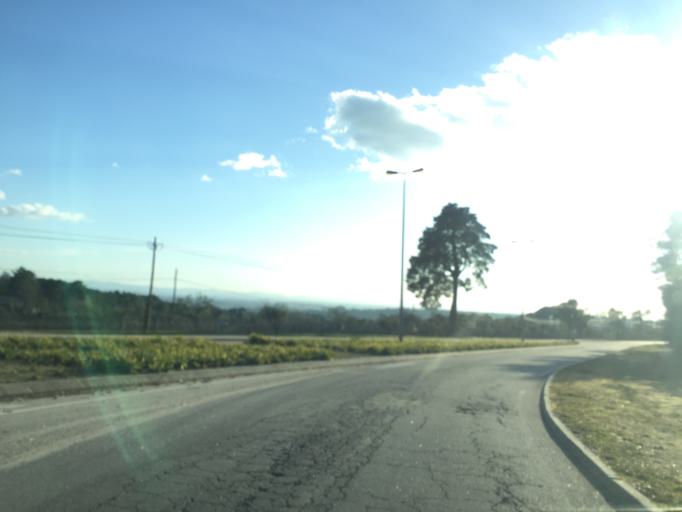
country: PT
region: Viseu
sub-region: Nelas
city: Nelas
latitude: 40.5216
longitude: -7.8665
